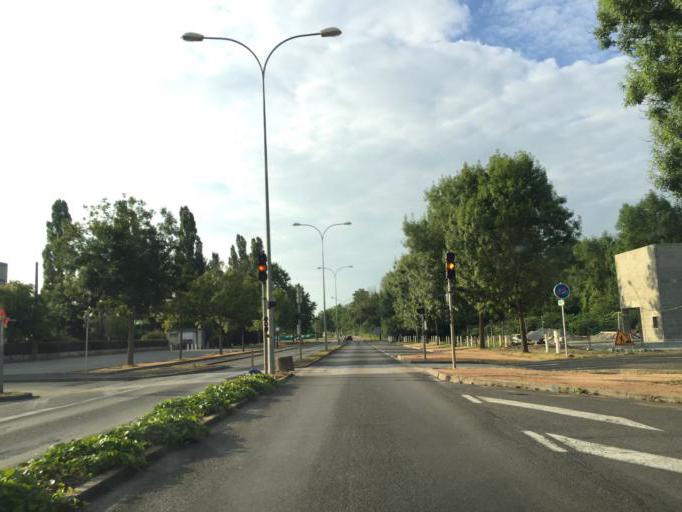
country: FR
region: Auvergne
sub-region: Departement de l'Allier
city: Creuzier-le-Vieux
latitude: 46.1491
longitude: 3.4142
